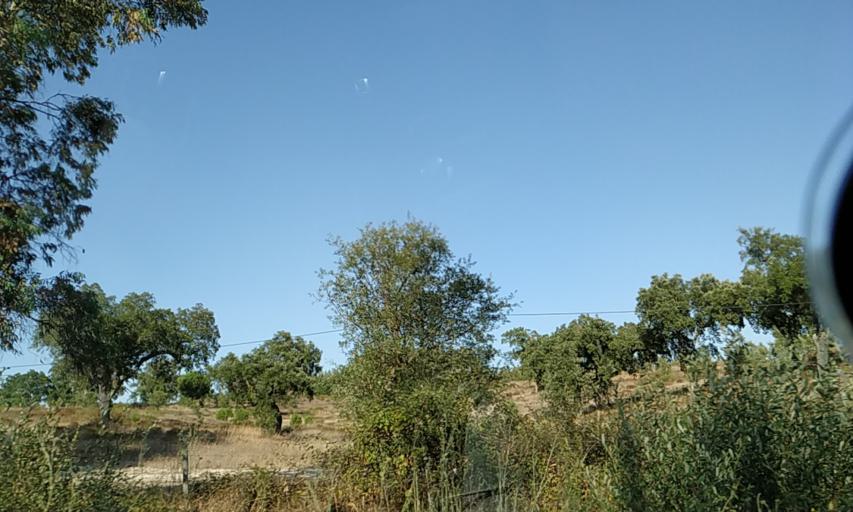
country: PT
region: Santarem
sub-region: Almeirim
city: Fazendas de Almeirim
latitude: 39.0700
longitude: -8.5651
